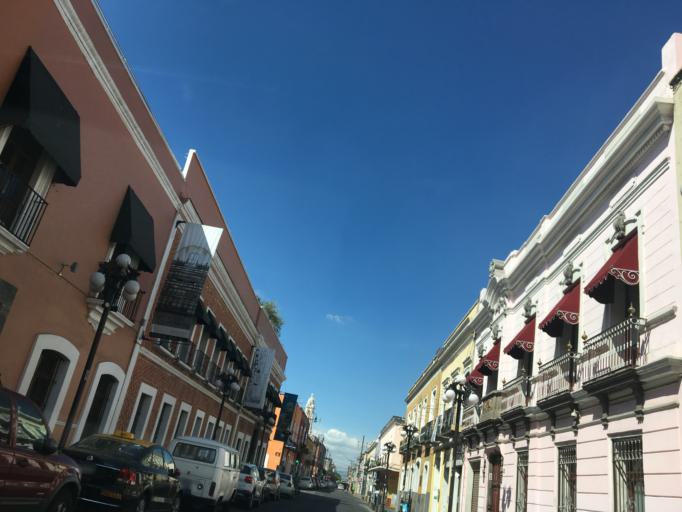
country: MX
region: Puebla
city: Puebla
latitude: 19.0412
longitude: -98.1986
